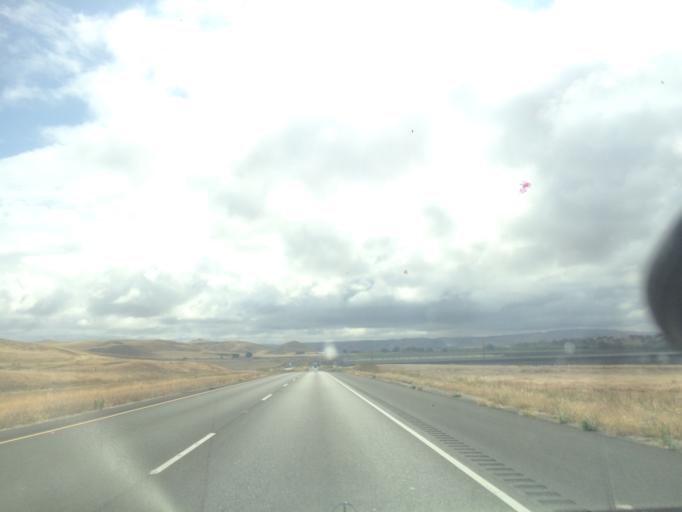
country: US
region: California
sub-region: San Luis Obispo County
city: Shandon
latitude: 35.6609
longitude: -120.4449
